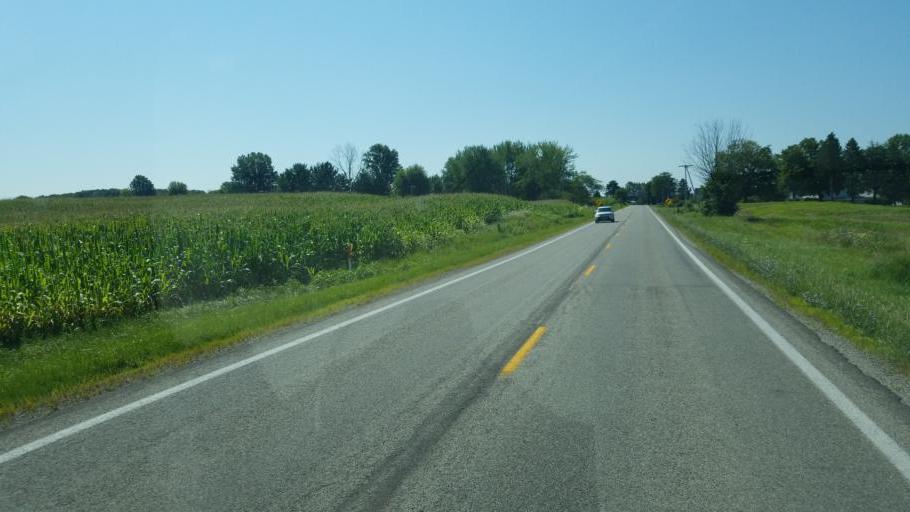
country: US
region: Ohio
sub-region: Morrow County
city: Mount Gilead
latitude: 40.5288
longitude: -82.8185
